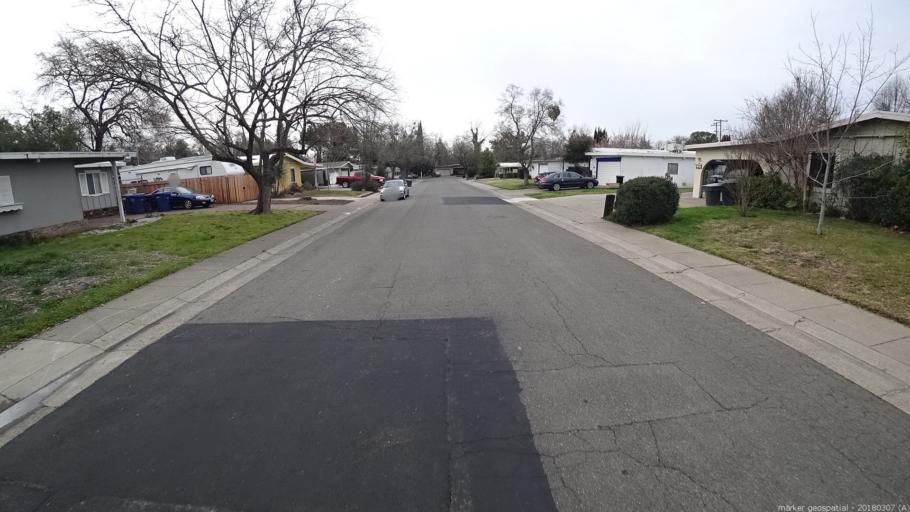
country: US
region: California
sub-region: Sacramento County
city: Carmichael
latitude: 38.6303
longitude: -121.3488
